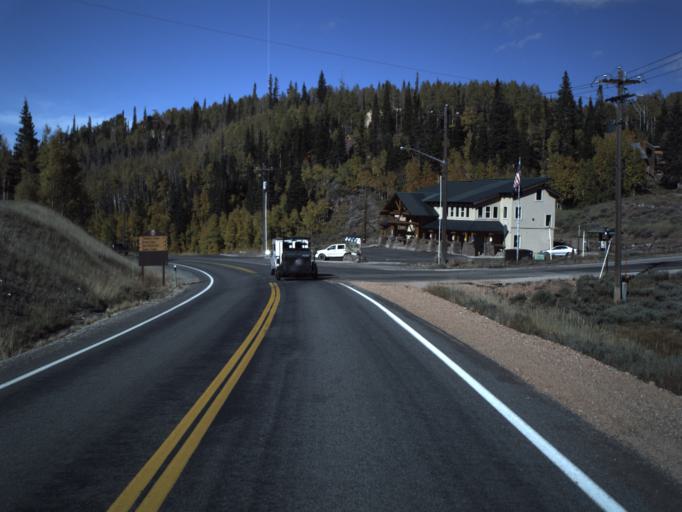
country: US
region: Utah
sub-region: Iron County
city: Parowan
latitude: 37.6976
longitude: -112.8454
